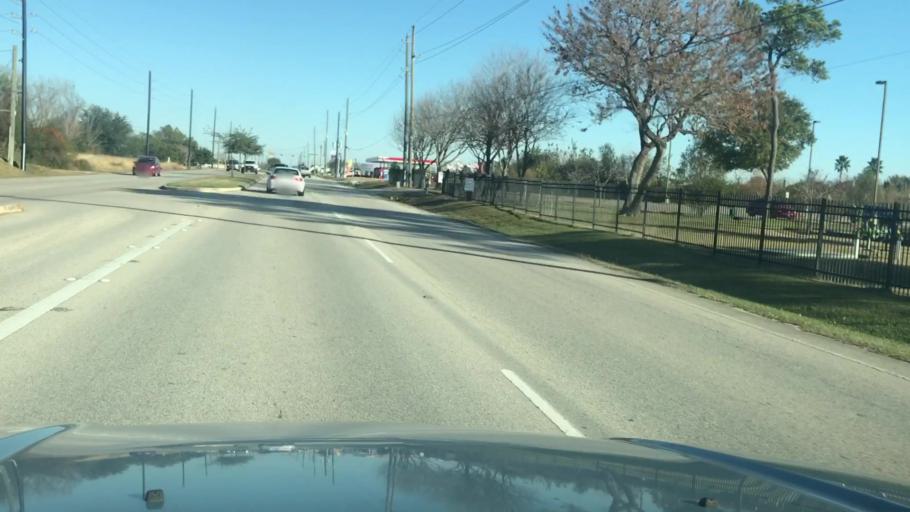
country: US
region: Texas
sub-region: Harris County
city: Katy
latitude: 29.8317
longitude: -95.7485
